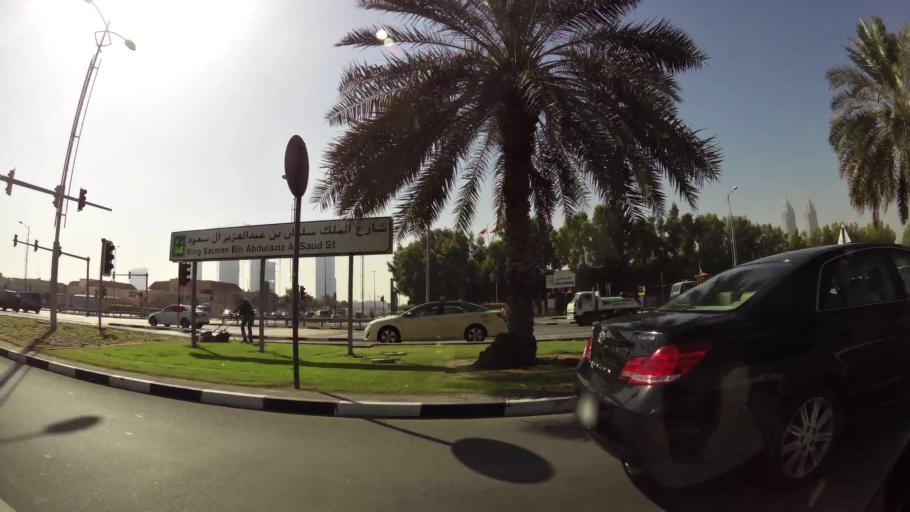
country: AE
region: Dubai
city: Dubai
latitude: 25.1118
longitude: 55.1682
